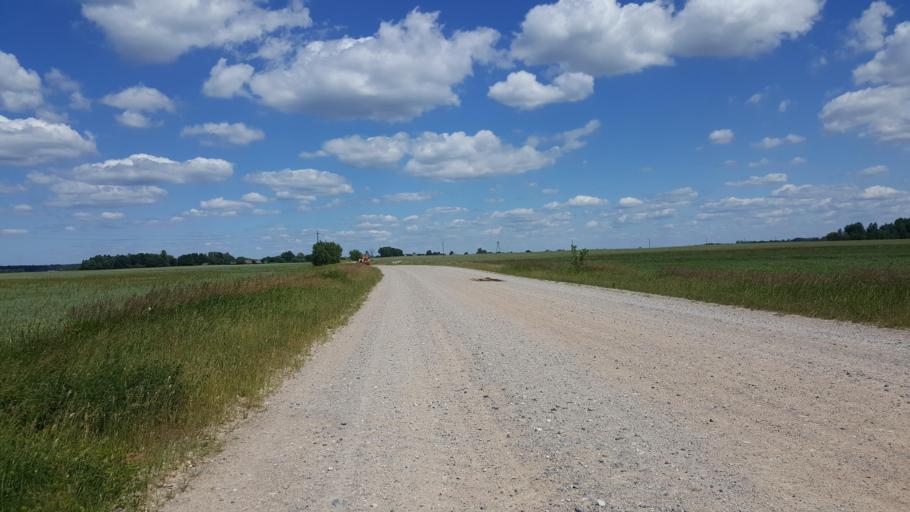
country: PL
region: Podlasie
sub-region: Powiat hajnowski
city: Czeremcha
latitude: 52.4934
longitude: 23.4580
